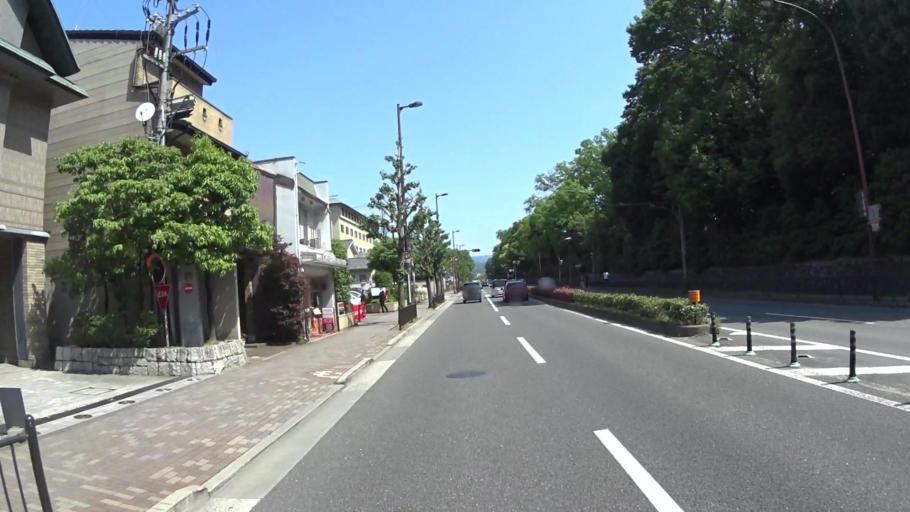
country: JP
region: Kyoto
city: Kyoto
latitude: 35.0231
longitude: 135.7592
